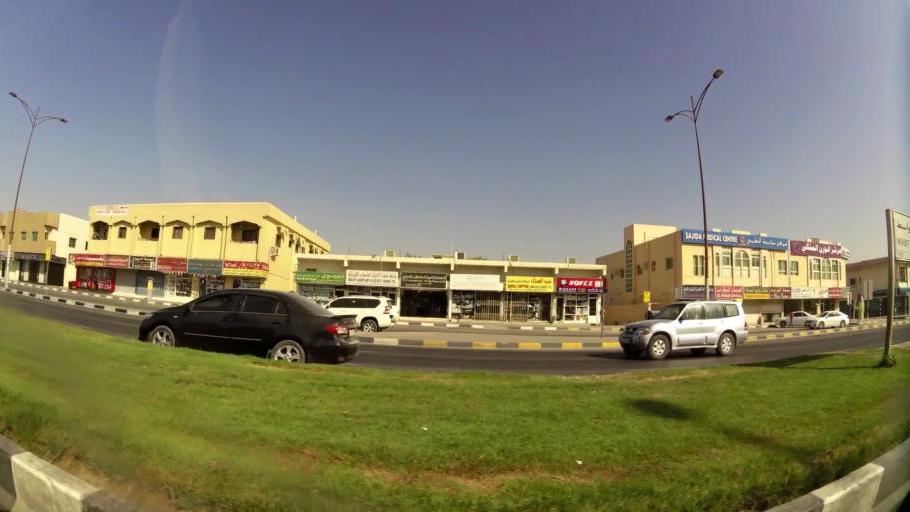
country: AE
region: Ash Shariqah
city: Sharjah
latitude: 25.3392
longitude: 55.4281
